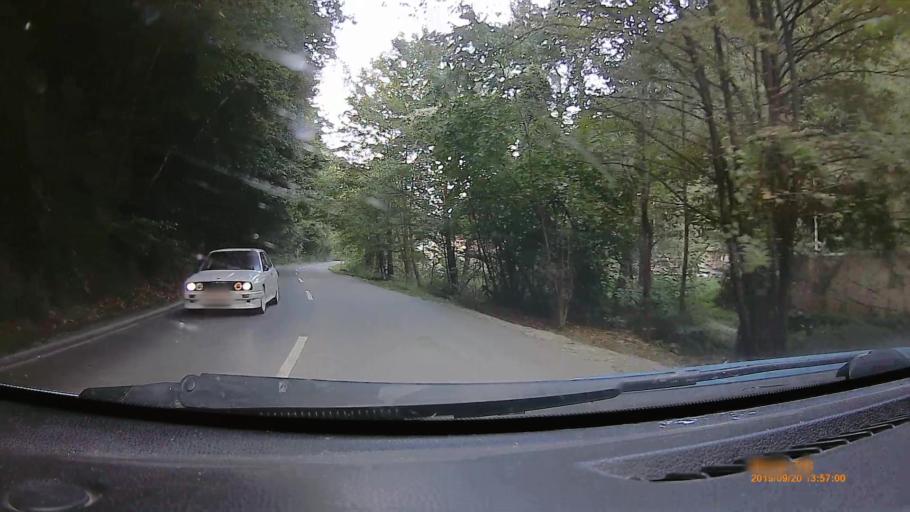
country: HU
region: Borsod-Abauj-Zemplen
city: Sajobabony
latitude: 48.0896
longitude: 20.6198
